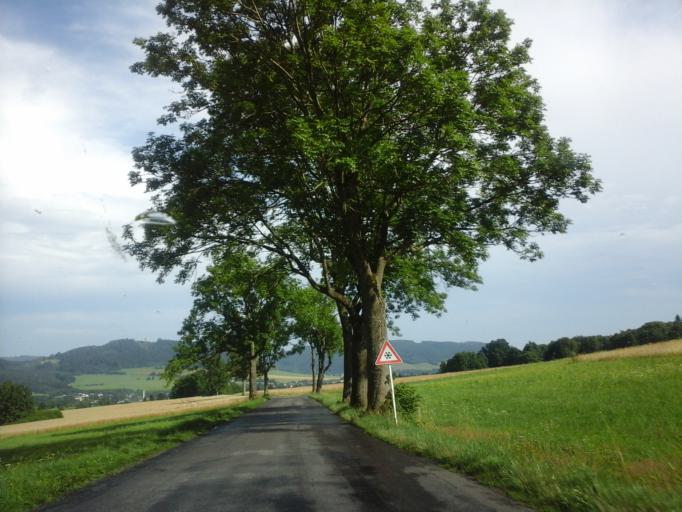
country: CZ
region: Pardubicky
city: Cervena Voda
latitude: 50.0530
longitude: 16.7204
